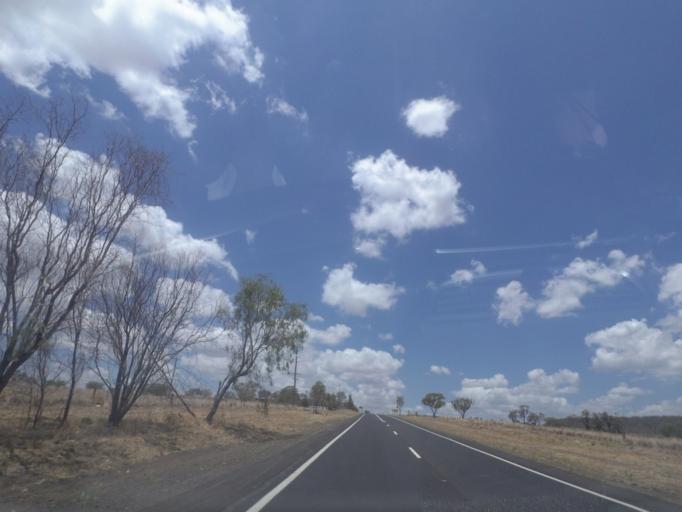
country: AU
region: Queensland
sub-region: Toowoomba
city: Top Camp
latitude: -27.7273
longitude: 151.9118
